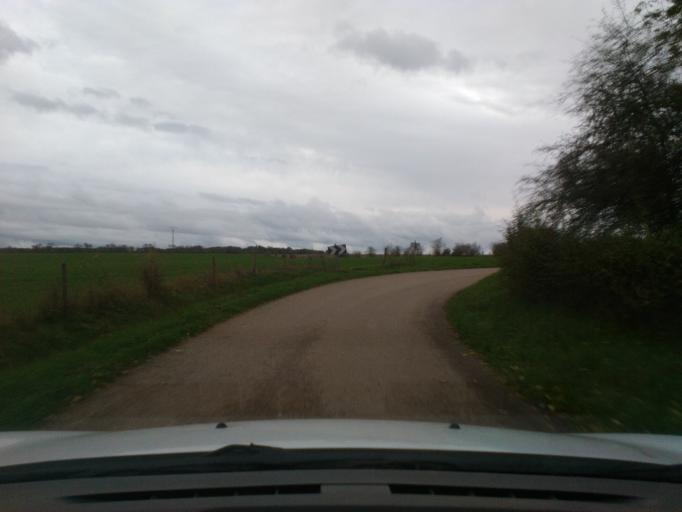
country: FR
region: Lorraine
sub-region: Departement des Vosges
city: Mirecourt
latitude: 48.3485
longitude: 6.0647
